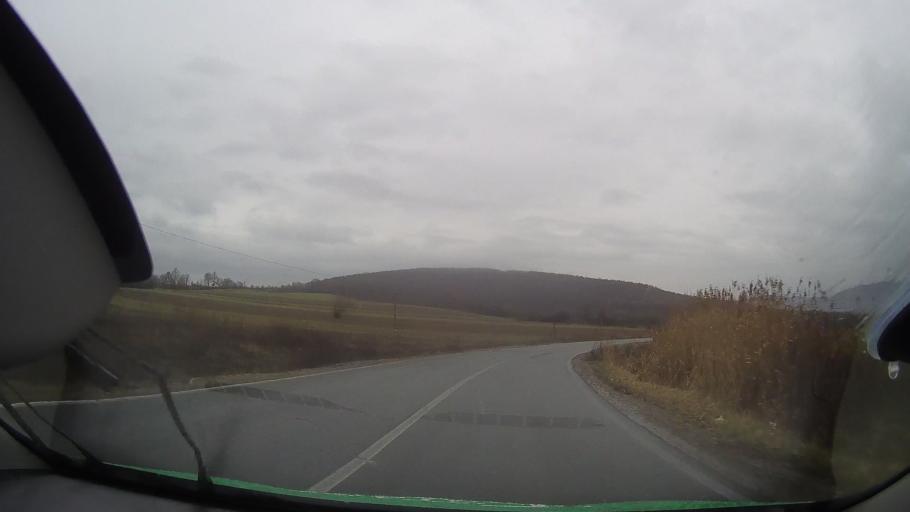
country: RO
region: Bihor
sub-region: Comuna Rabagani
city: Rabagani
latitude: 46.7284
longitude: 22.2352
